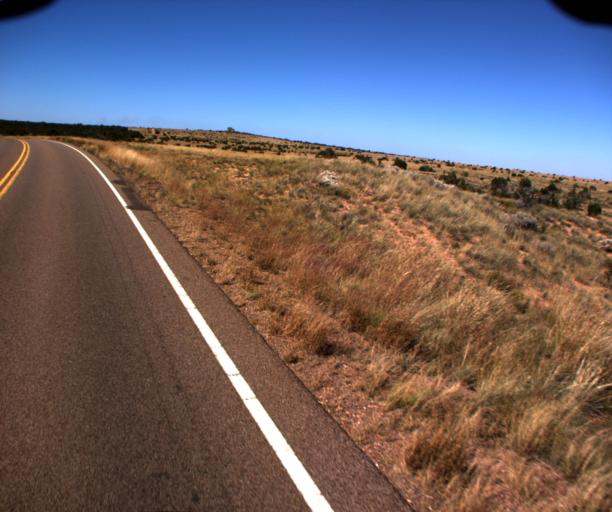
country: US
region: Arizona
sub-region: Navajo County
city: Taylor
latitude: 34.4829
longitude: -110.3320
